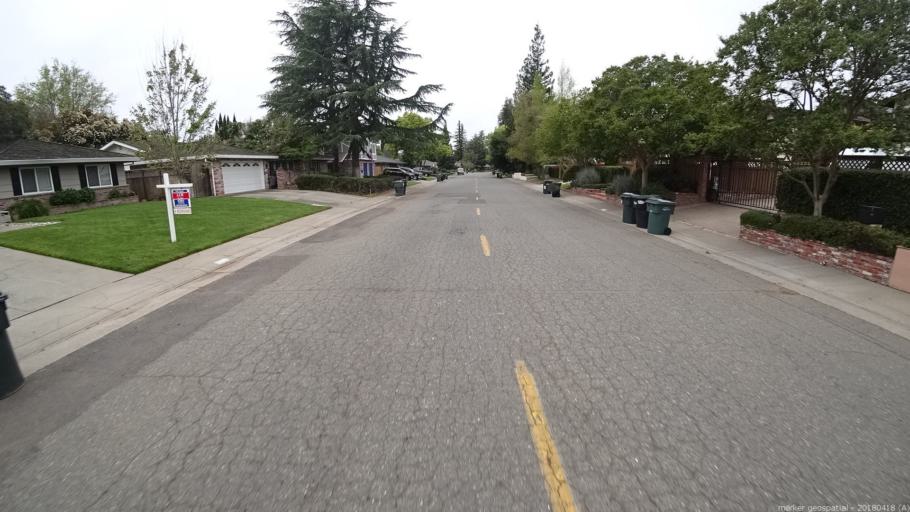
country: US
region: California
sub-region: Sacramento County
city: La Riviera
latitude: 38.5778
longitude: -121.3305
